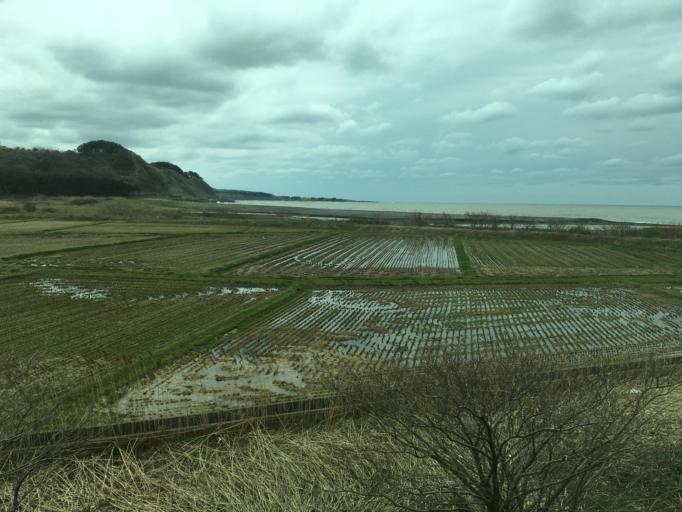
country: JP
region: Aomori
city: Shimokizukuri
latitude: 40.6871
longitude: 139.9694
